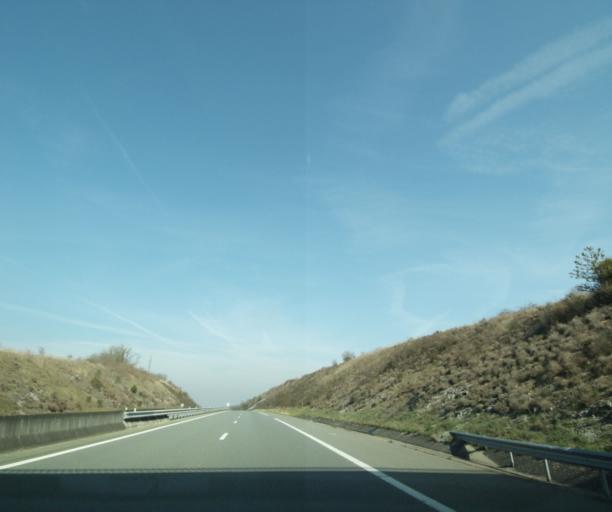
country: FR
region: Midi-Pyrenees
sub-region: Departement du Lot
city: Le Vigan
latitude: 44.7093
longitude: 1.5715
